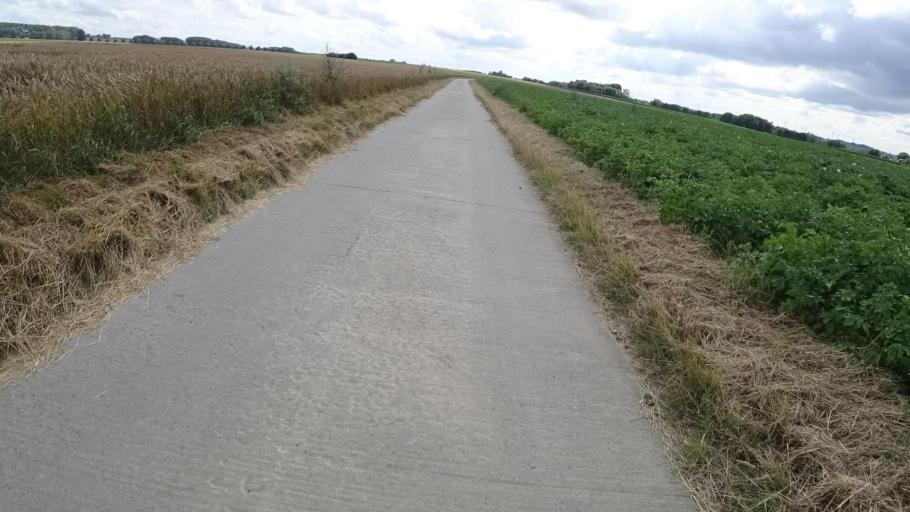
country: BE
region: Wallonia
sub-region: Province de Namur
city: Sombreffe
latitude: 50.5716
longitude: 4.5738
